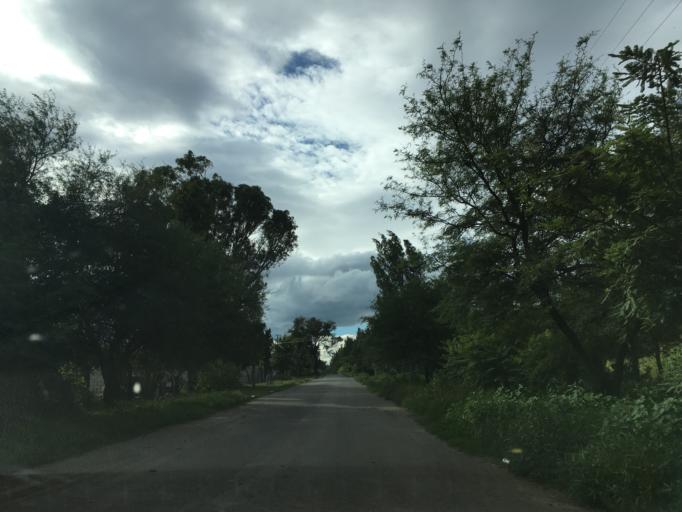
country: MX
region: Guanajuato
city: Iramuco
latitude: 19.9632
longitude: -100.9386
